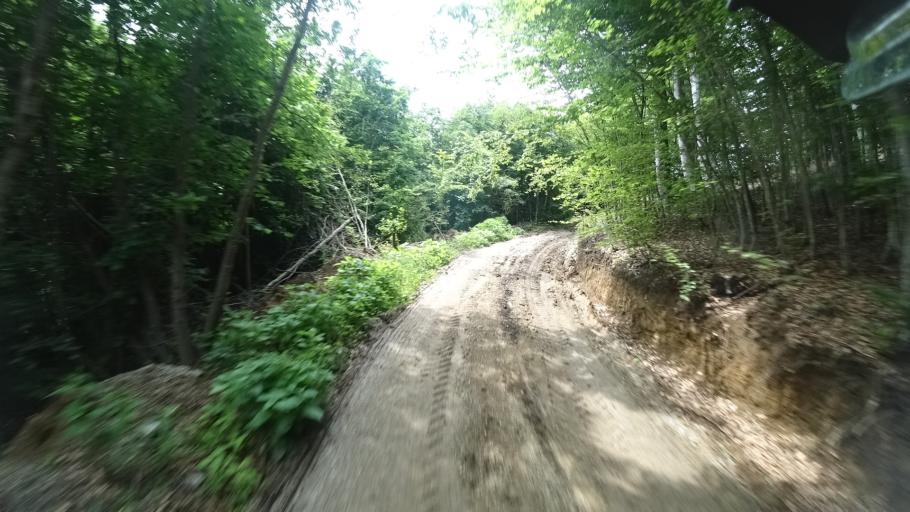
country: HR
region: Karlovacka
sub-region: Grad Karlovac
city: Slunj
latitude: 45.2031
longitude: 15.6278
